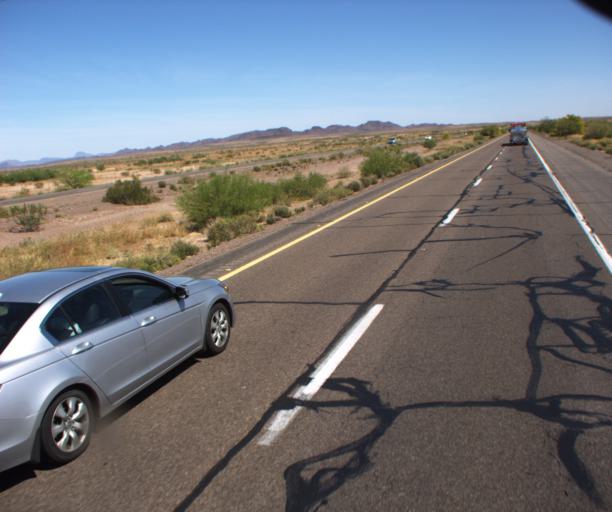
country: US
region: Arizona
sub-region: Maricopa County
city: Gila Bend
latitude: 32.8801
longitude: -113.1049
